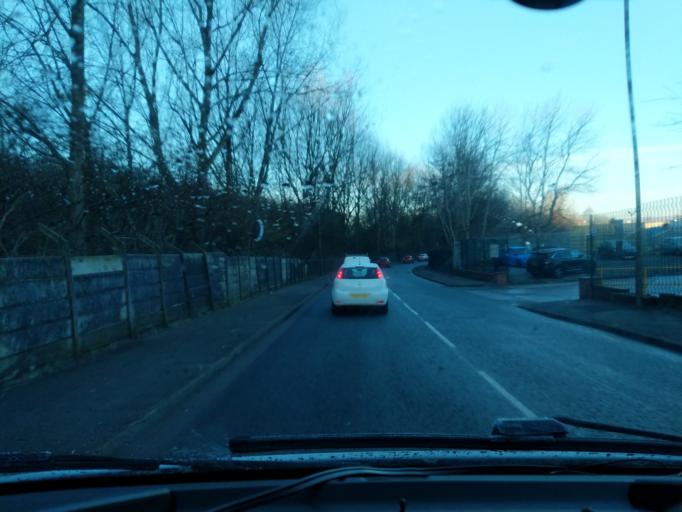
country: GB
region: England
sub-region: St. Helens
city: St Helens
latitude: 53.4687
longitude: -2.7347
